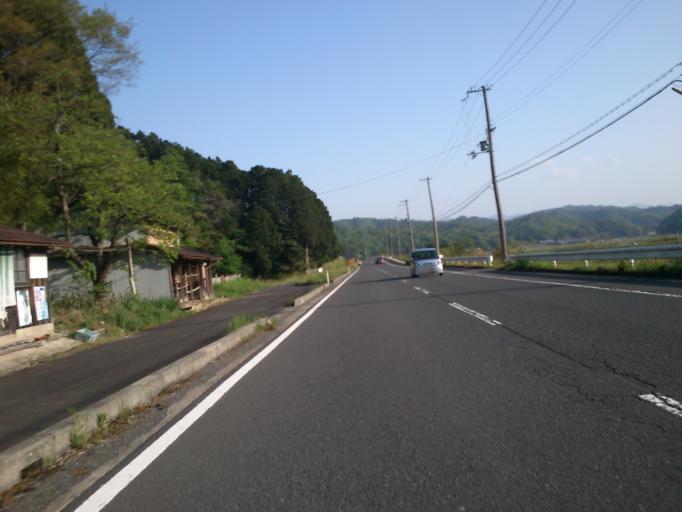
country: JP
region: Kyoto
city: Miyazu
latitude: 35.6043
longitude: 135.1383
